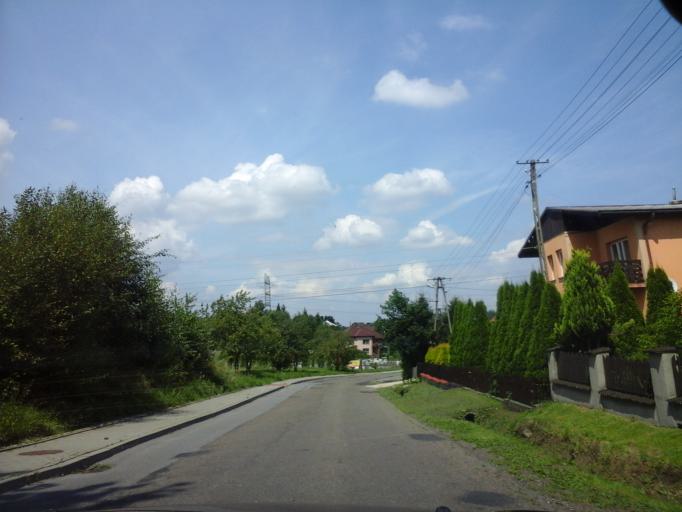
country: PL
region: Lesser Poland Voivodeship
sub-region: Powiat wadowicki
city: Bachowice
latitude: 49.9768
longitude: 19.5021
